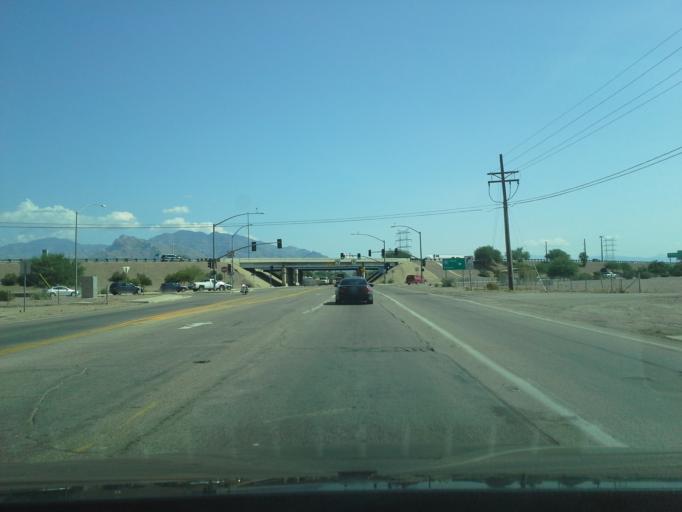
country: US
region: Arizona
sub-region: Pima County
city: Flowing Wells
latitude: 32.3375
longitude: -111.0686
